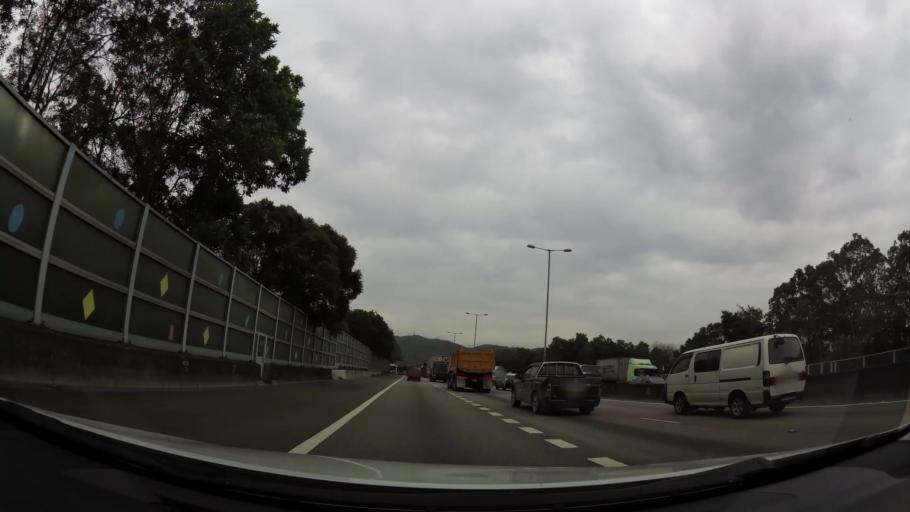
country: HK
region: Yuen Long
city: Yuen Long Kau Hui
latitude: 22.4344
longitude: 114.0284
